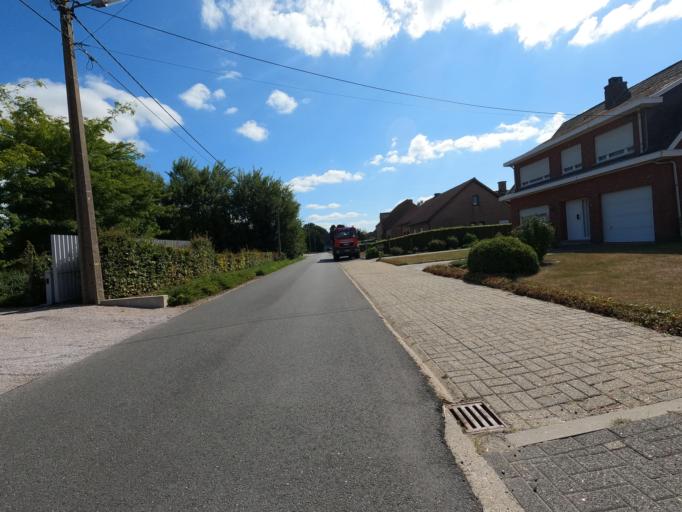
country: BE
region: Flanders
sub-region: Provincie Antwerpen
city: Hulshout
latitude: 51.1009
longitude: 4.7994
